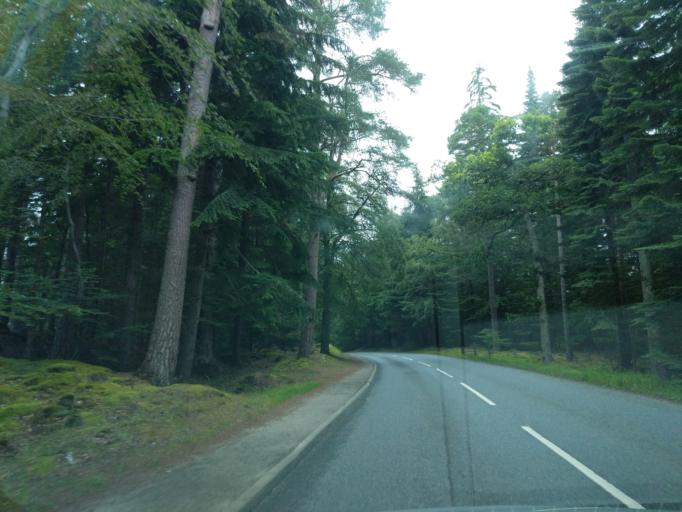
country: GB
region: Scotland
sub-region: Highland
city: Grantown on Spey
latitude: 57.3242
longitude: -3.6064
